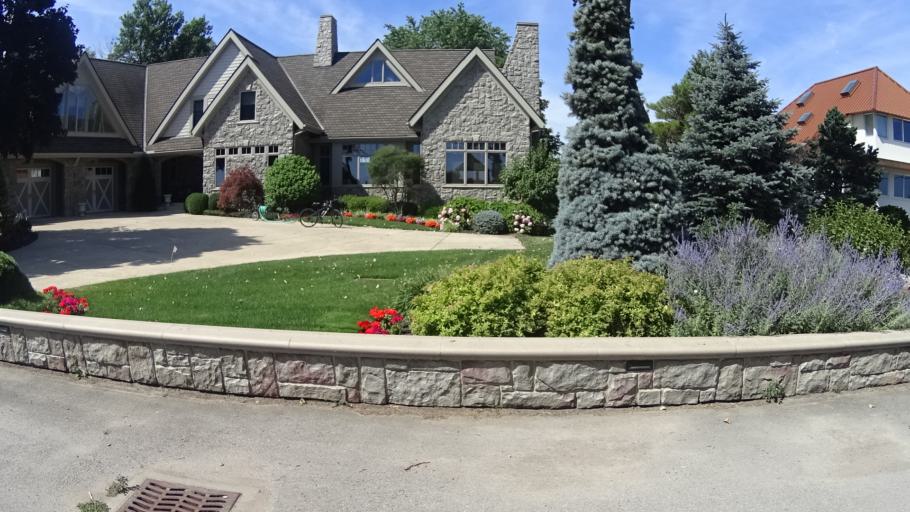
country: US
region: Ohio
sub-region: Erie County
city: Sandusky
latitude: 41.4561
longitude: -82.6529
